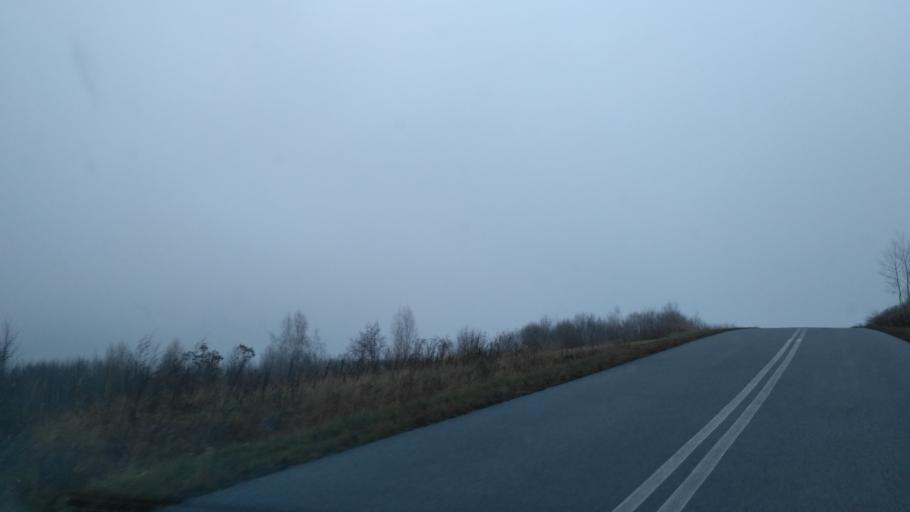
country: PL
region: Subcarpathian Voivodeship
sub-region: Powiat jaroslawski
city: Jodlowka
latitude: 49.8877
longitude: 22.4766
